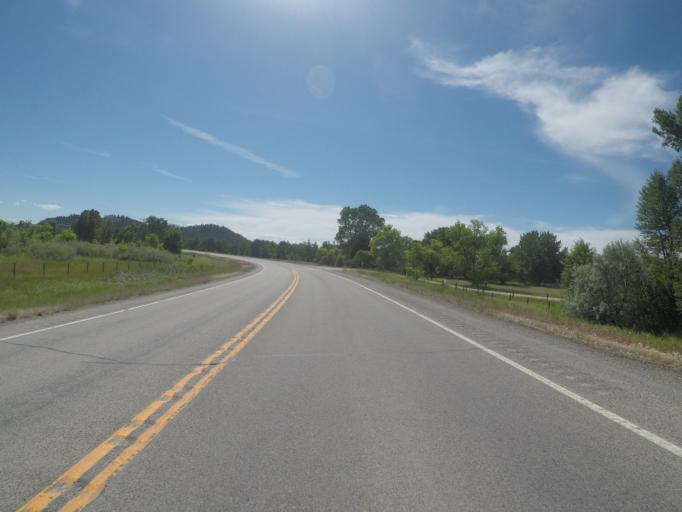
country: US
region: Montana
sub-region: Stillwater County
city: Columbus
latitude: 45.6326
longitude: -109.2746
